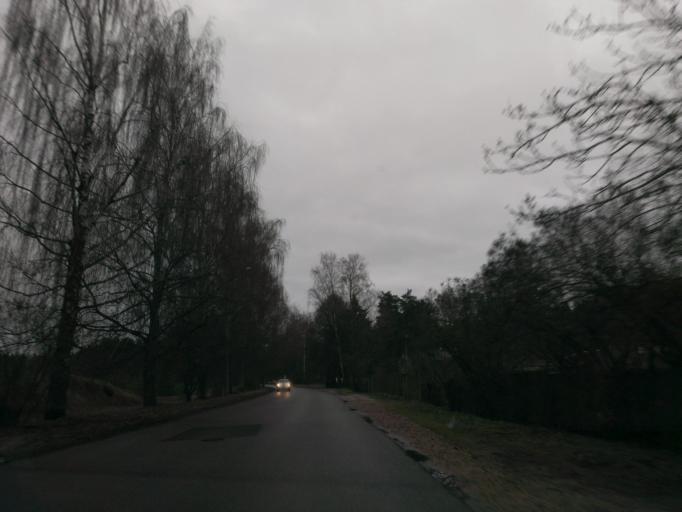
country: LV
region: Riga
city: Bergi
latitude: 56.9960
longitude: 24.2794
